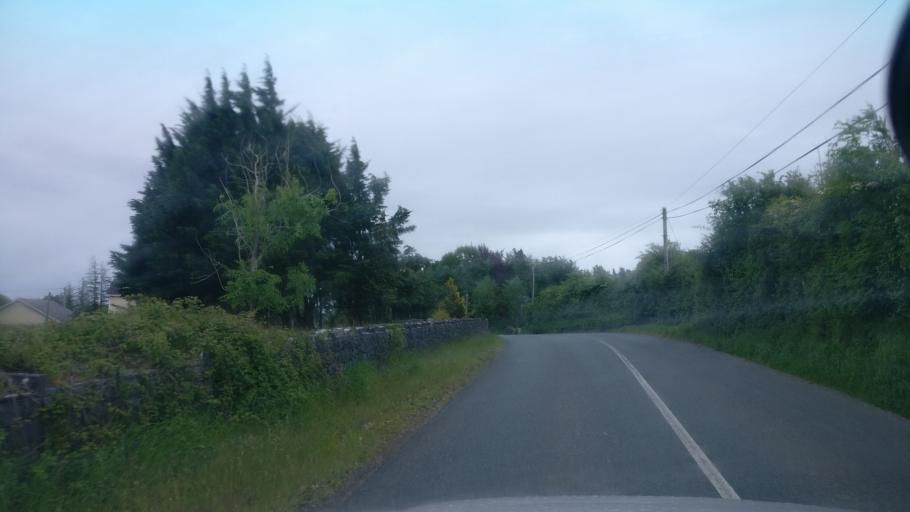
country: IE
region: Connaught
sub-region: County Galway
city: Gort
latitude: 53.0681
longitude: -8.7813
